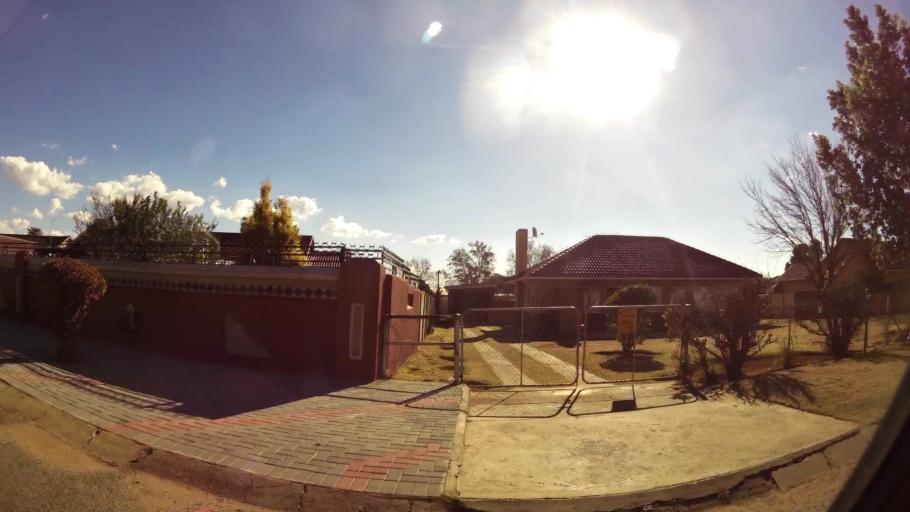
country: ZA
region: Gauteng
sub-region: West Rand District Municipality
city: Carletonville
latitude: -26.3731
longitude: 27.3988
